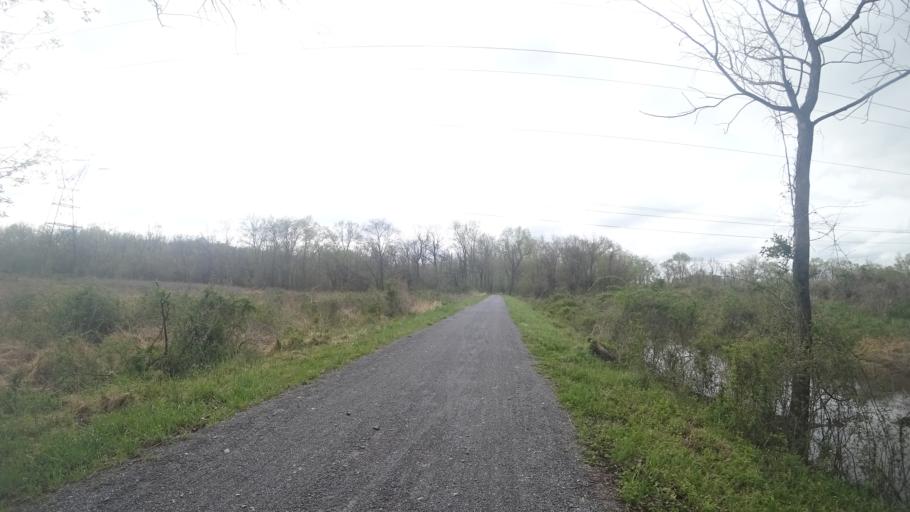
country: US
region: Virginia
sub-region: Loudoun County
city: Belmont
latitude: 39.1202
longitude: -77.5013
